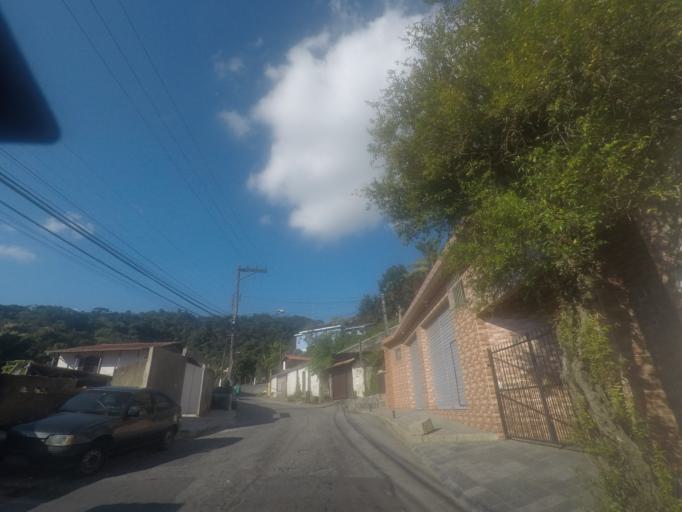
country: BR
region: Rio de Janeiro
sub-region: Petropolis
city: Petropolis
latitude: -22.5069
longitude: -43.1584
